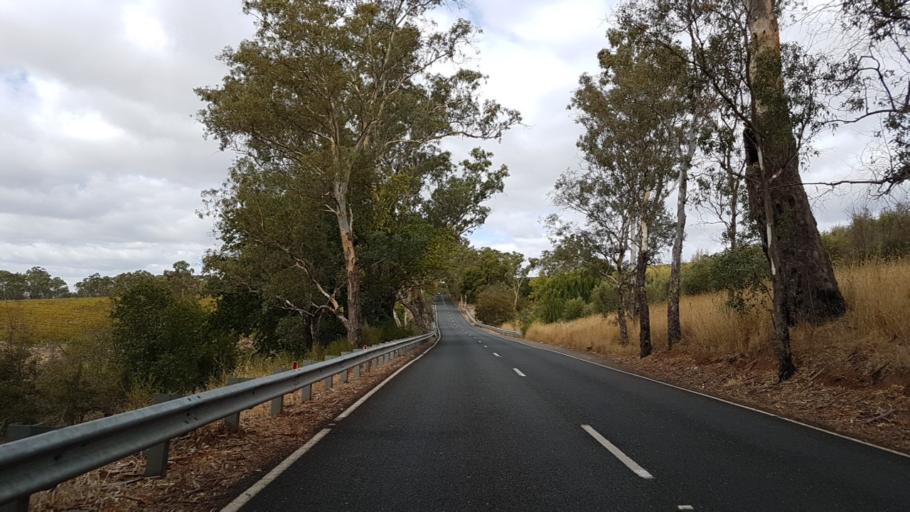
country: AU
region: South Australia
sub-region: Adelaide Hills
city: Gumeracha
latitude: -34.8199
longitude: 138.8637
